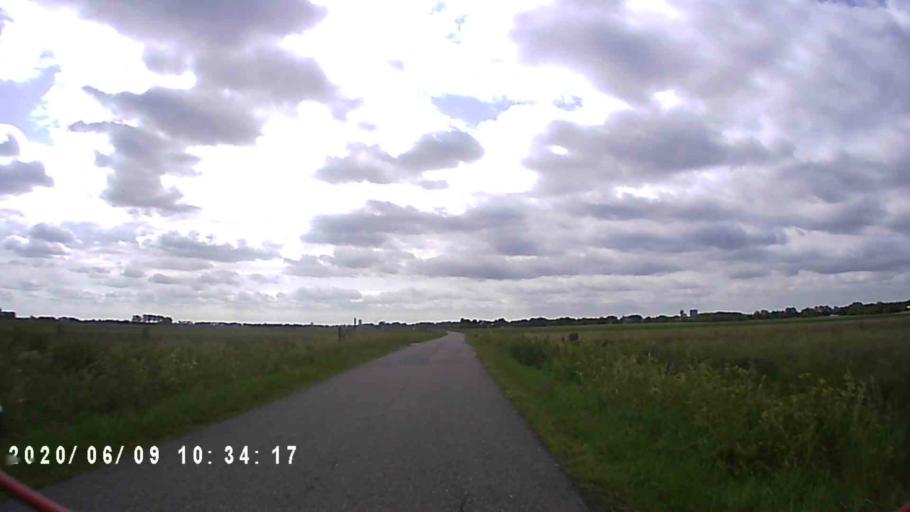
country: NL
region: Groningen
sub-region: Gemeente Zuidhorn
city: Aduard
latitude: 53.2647
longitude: 6.5164
